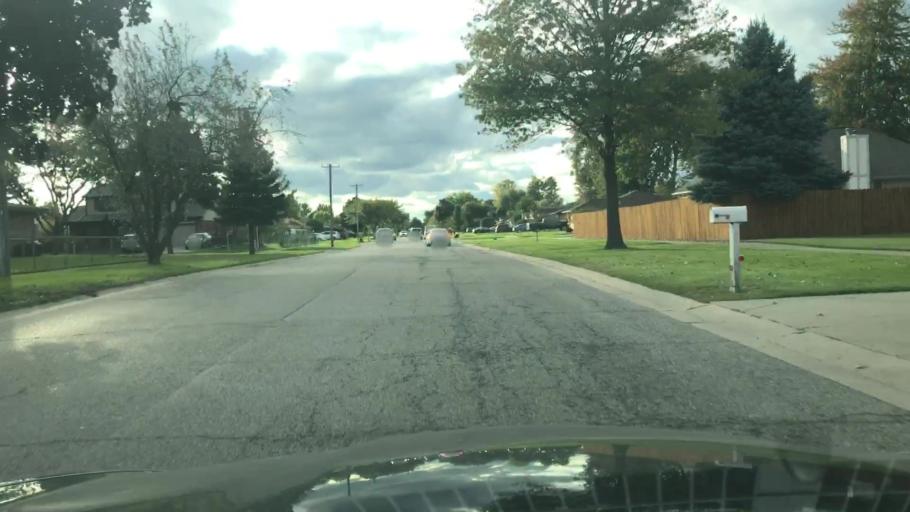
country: US
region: Michigan
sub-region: Macomb County
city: Sterling Heights
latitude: 42.5724
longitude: -83.0536
